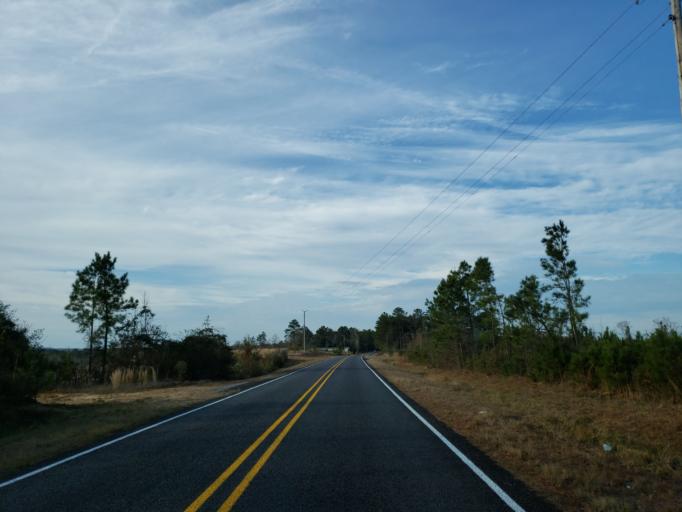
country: US
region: Mississippi
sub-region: Wayne County
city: Belmont
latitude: 31.4911
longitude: -88.5038
